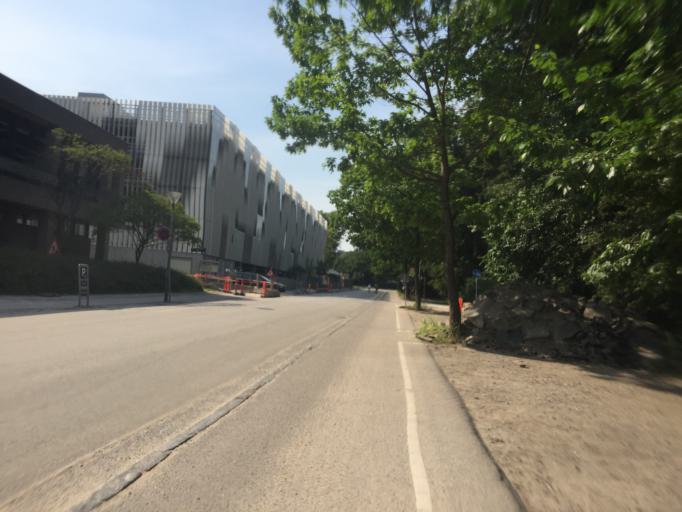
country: DK
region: Capital Region
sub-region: Kobenhavn
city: Copenhagen
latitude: 55.6985
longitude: 12.5666
